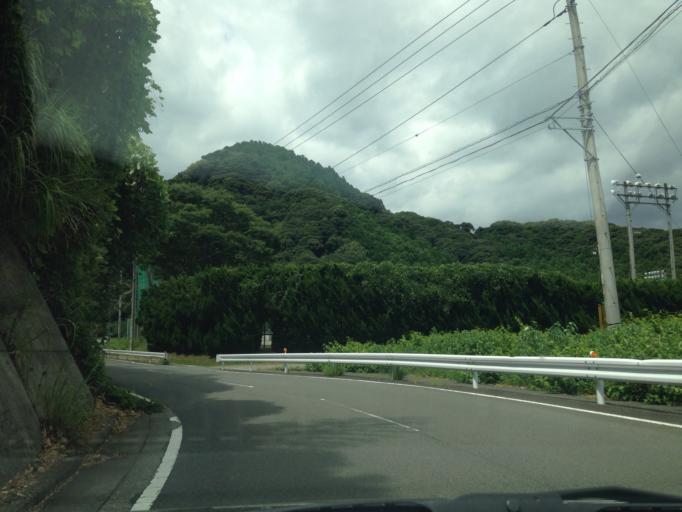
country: JP
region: Shizuoka
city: Shimoda
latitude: 34.6451
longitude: 138.8201
